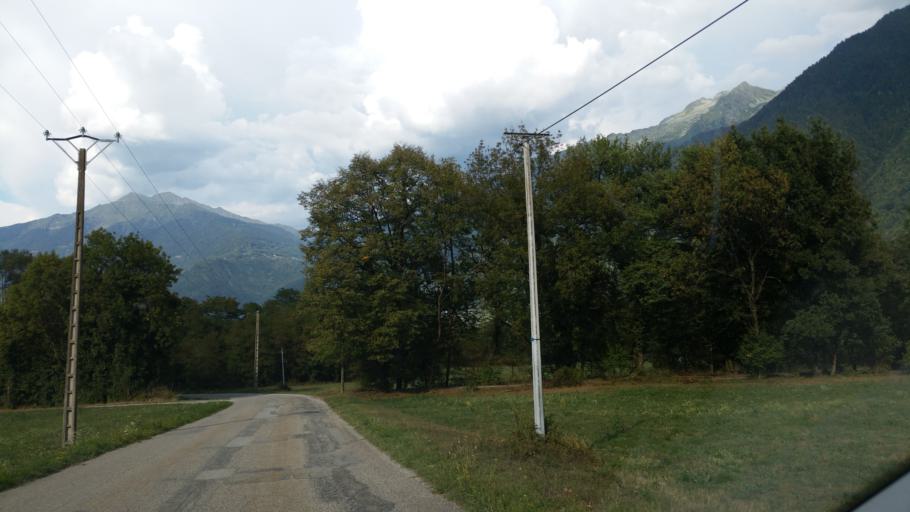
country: FR
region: Rhone-Alpes
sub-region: Departement de la Savoie
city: Saint-Remy-de-Maurienne
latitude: 45.4764
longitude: 6.2818
